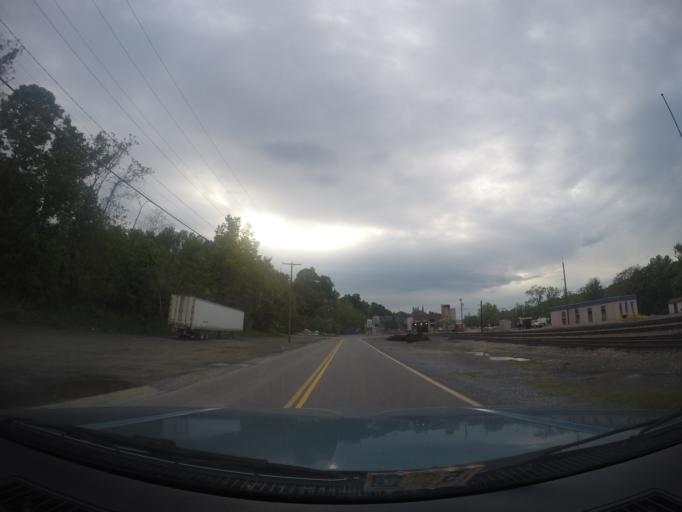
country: US
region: Virginia
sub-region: City of Lynchburg
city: Lynchburg
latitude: 37.3982
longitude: -79.1222
